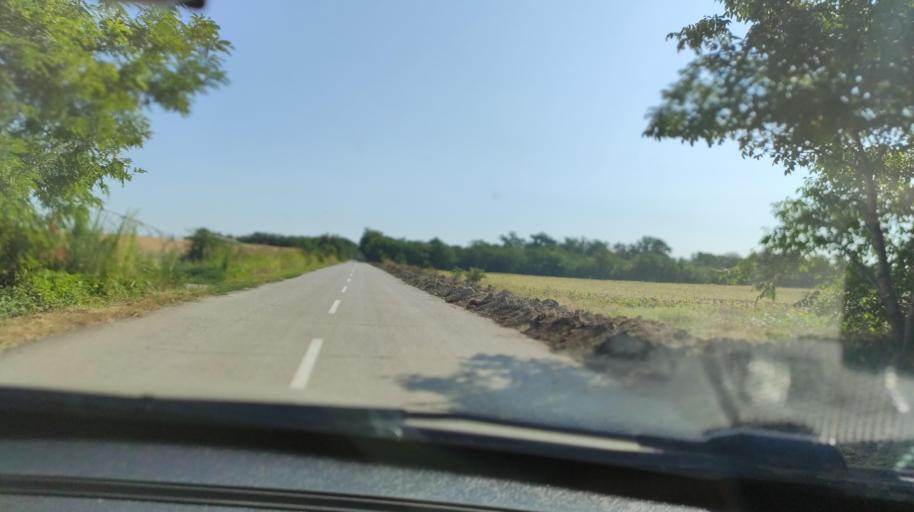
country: RS
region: Autonomna Pokrajina Vojvodina
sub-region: Severnobacki Okrug
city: Backa Topola
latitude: 45.8644
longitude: 19.6032
